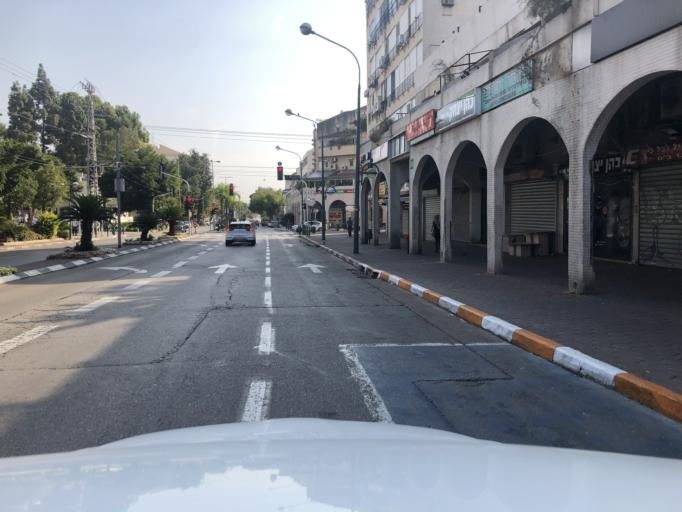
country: IL
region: Central District
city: Kfar Saba
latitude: 32.1748
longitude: 34.9104
